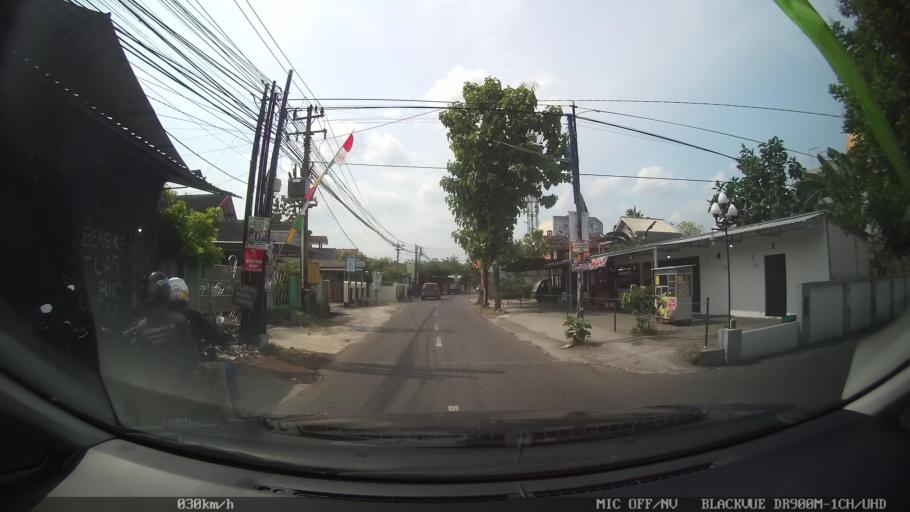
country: ID
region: Daerah Istimewa Yogyakarta
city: Depok
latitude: -7.8004
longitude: 110.4164
